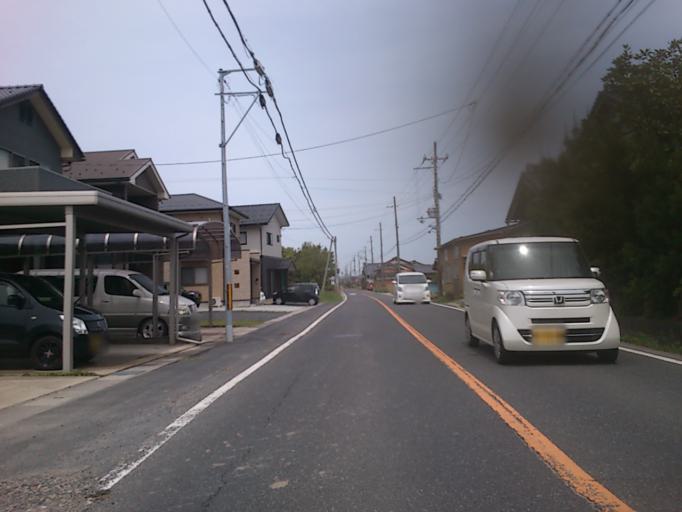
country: JP
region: Kyoto
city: Miyazu
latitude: 35.5959
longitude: 135.0962
